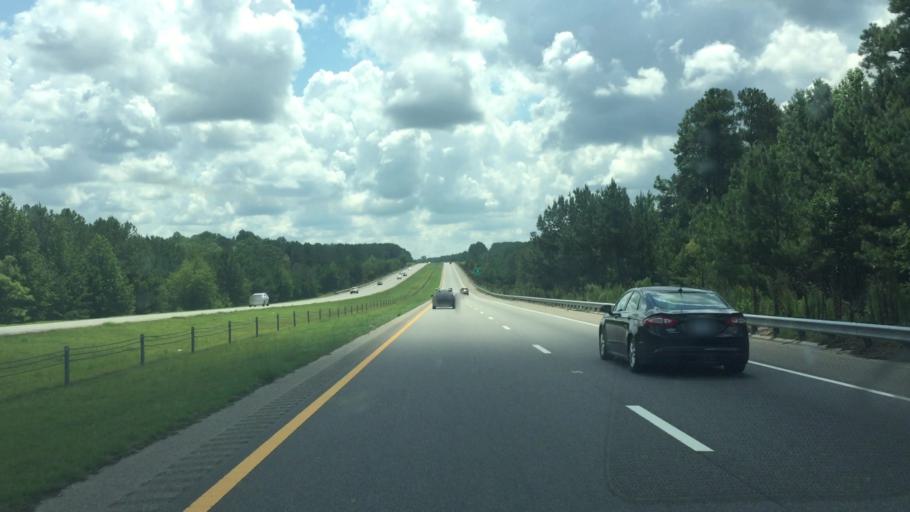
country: US
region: North Carolina
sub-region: Richmond County
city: East Rockingham
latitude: 34.8802
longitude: -79.7784
